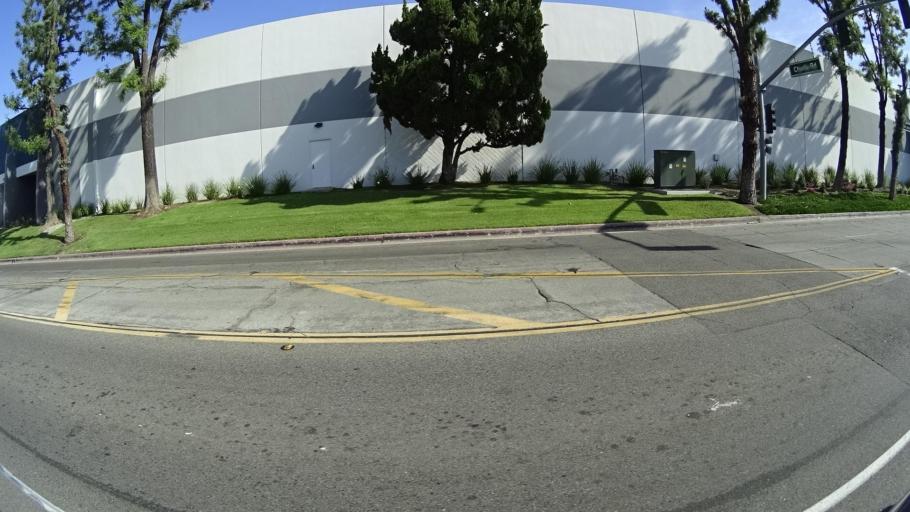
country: US
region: California
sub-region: Los Angeles County
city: South San Jose Hills
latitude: 33.9992
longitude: -117.8952
